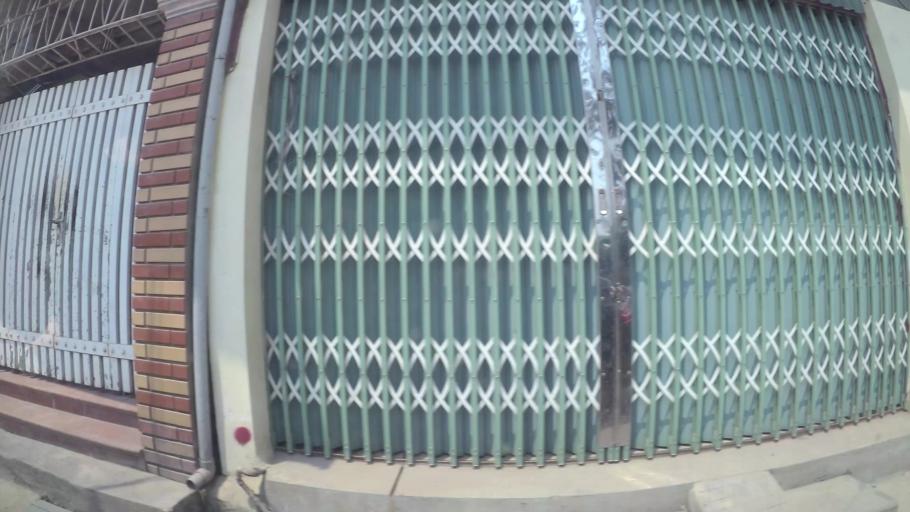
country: VN
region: Ha Noi
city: Van Dien
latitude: 20.9524
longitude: 105.8279
